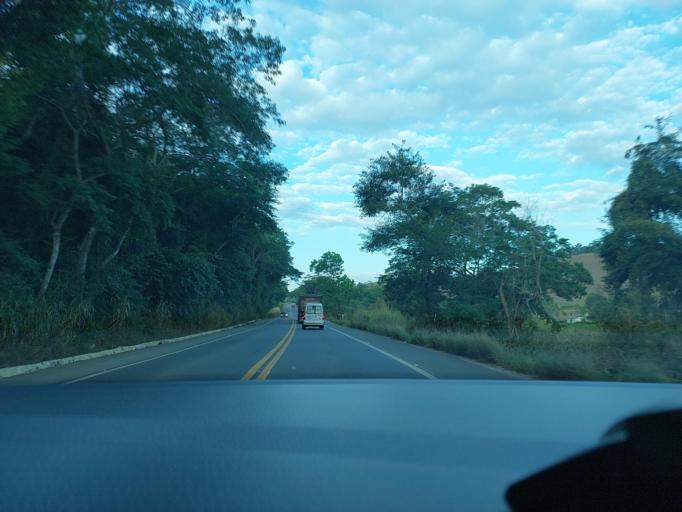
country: BR
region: Minas Gerais
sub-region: Muriae
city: Muriae
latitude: -21.1491
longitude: -42.1598
